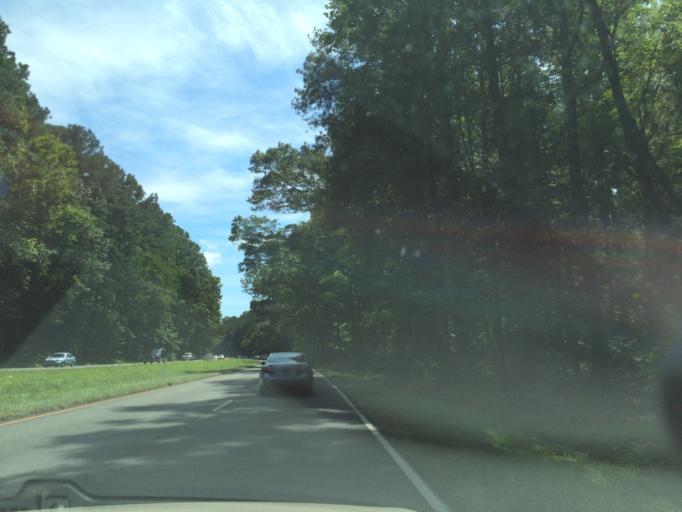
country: US
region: Virginia
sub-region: York County
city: Yorktown
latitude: 37.2106
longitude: -76.5127
